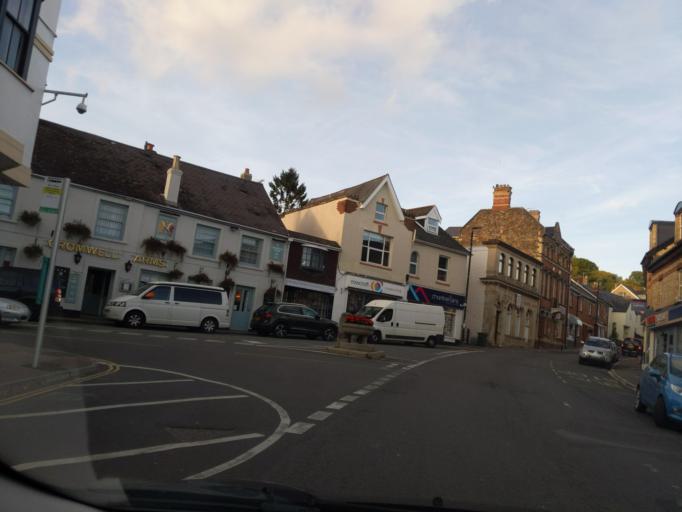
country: GB
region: England
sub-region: Devon
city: Bovey Tracey
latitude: 50.5937
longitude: -3.6749
